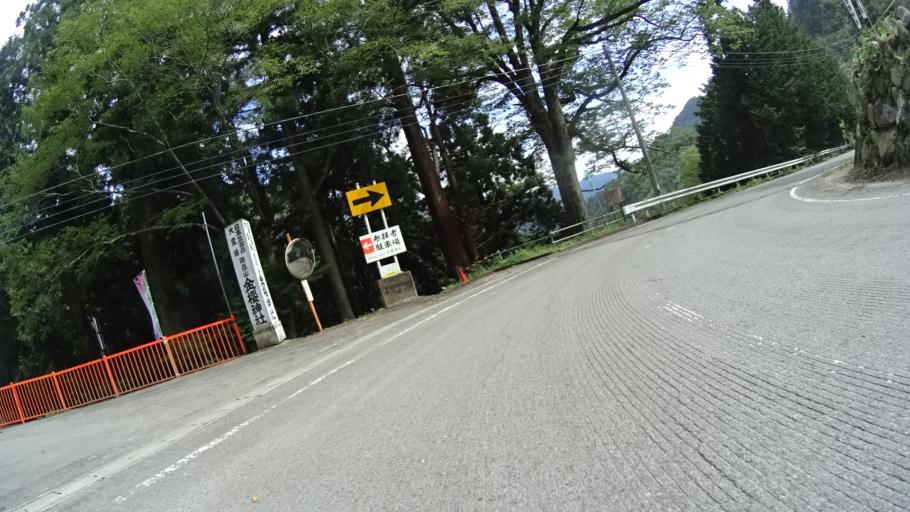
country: JP
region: Yamanashi
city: Kofu-shi
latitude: 35.7689
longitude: 138.5555
